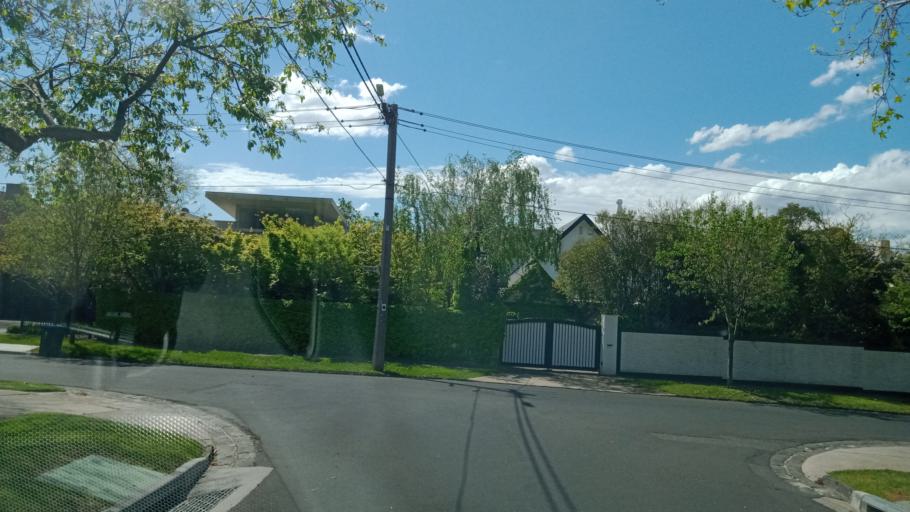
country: AU
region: Victoria
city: Toorak
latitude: -37.8425
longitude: 145.0333
